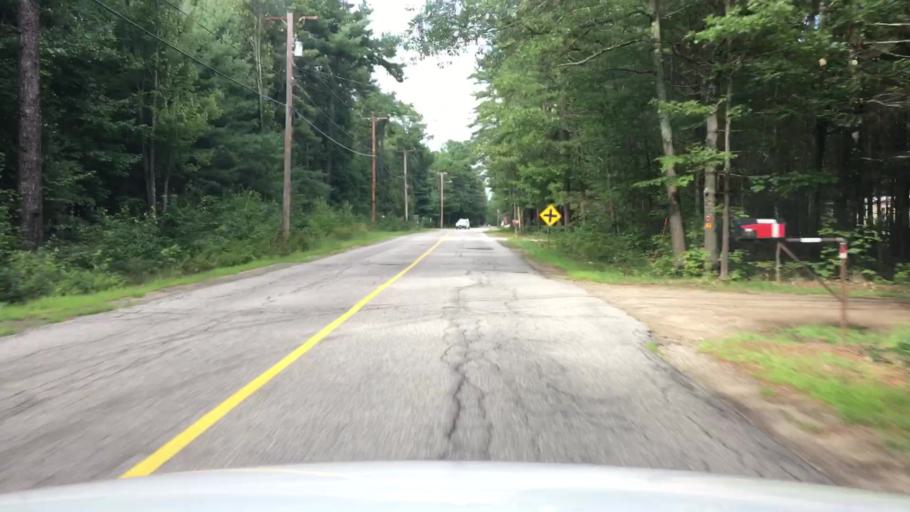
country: US
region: Maine
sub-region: York County
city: West Kennebunk
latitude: 43.4227
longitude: -70.6547
